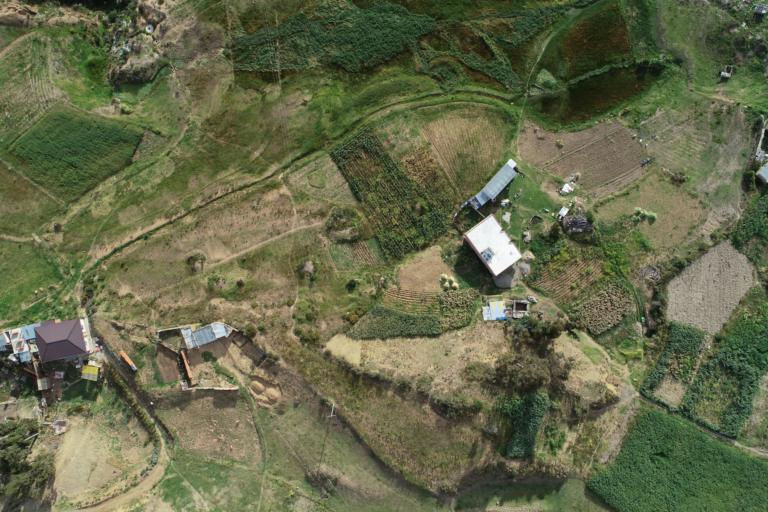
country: BO
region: La Paz
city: La Paz
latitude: -16.5472
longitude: -68.0013
